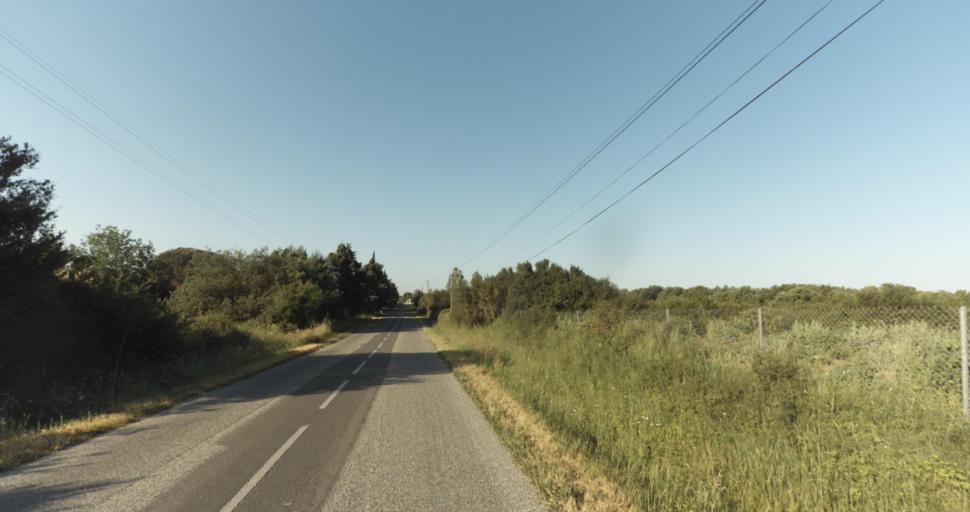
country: FR
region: Midi-Pyrenees
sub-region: Departement de la Haute-Garonne
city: Leguevin
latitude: 43.5720
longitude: 1.2351
